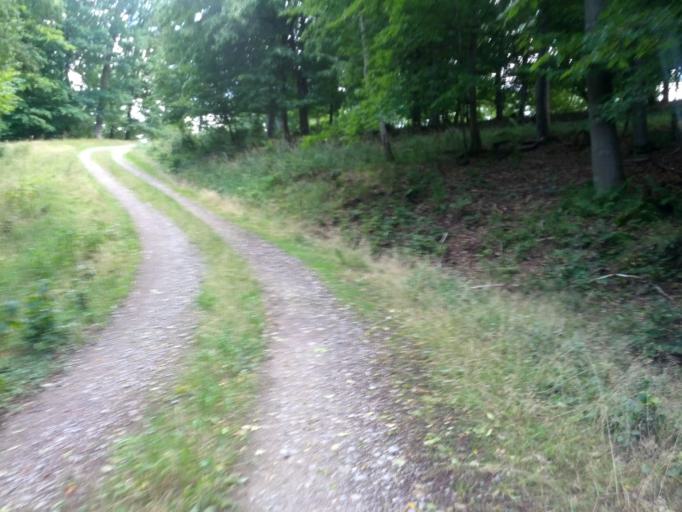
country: DE
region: Thuringia
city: Wolfsburg-Unkeroda
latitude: 50.9679
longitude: 10.2577
